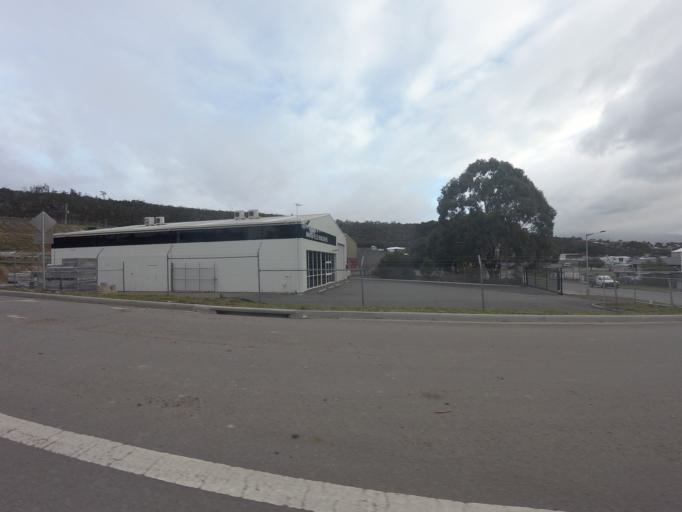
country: AU
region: Tasmania
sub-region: Clarence
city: Warrane
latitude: -42.8608
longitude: 147.4037
